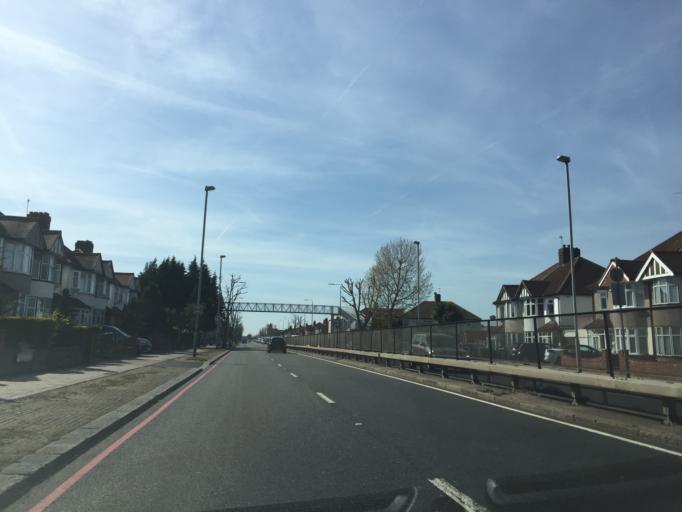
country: GB
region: England
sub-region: Greater London
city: Chislehurst
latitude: 51.4324
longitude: 0.0737
